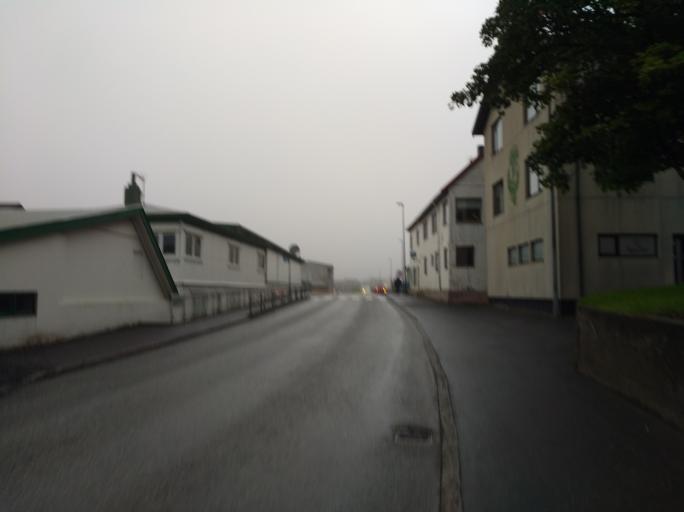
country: FO
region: Nordoyar
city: Klaksvik
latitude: 62.2267
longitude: -6.5896
